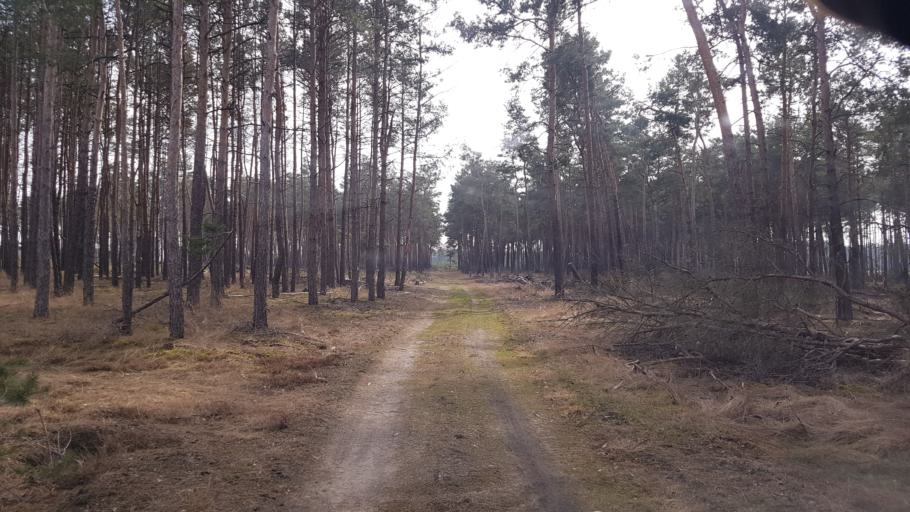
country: DE
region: Brandenburg
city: Schlieben
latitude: 51.6713
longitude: 13.3625
